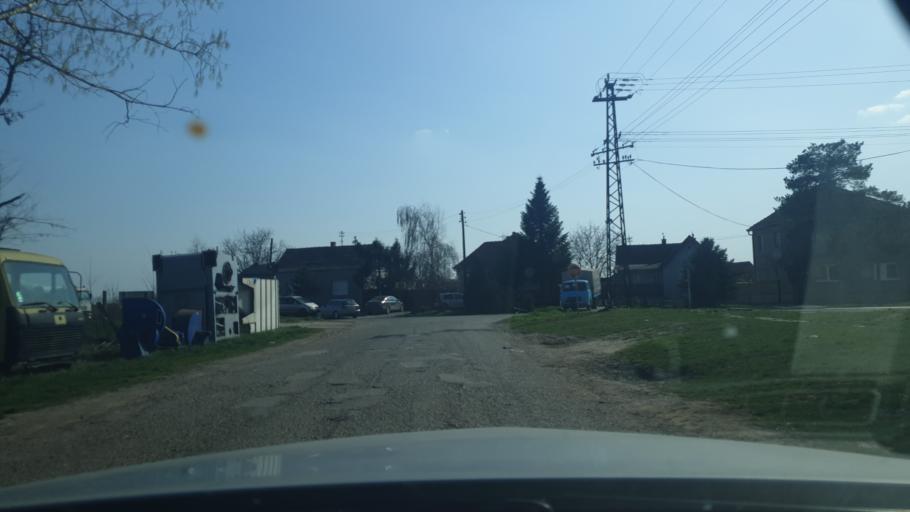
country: RS
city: Putinci
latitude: 45.0011
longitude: 19.9393
